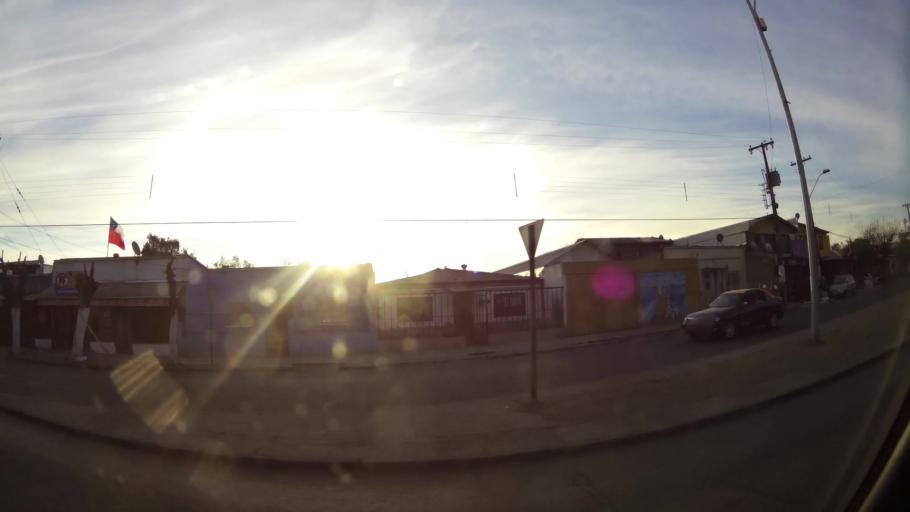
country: CL
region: Santiago Metropolitan
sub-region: Provincia de Santiago
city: Lo Prado
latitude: -33.4398
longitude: -70.7228
